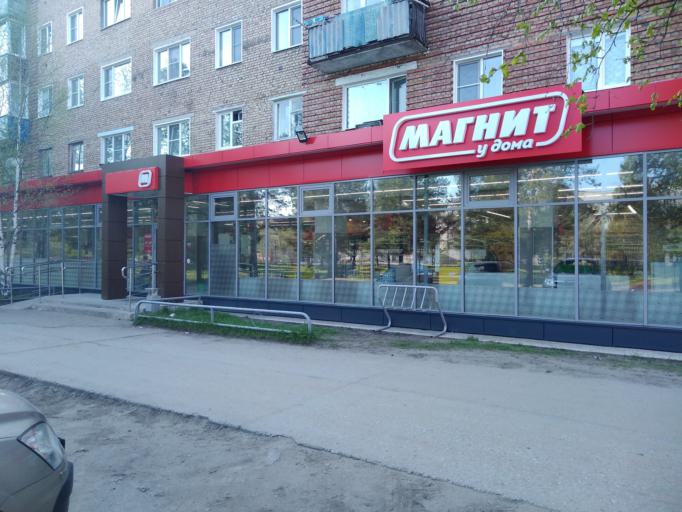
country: RU
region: Komi Republic
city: Pechora
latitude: 65.1100
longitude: 57.1572
